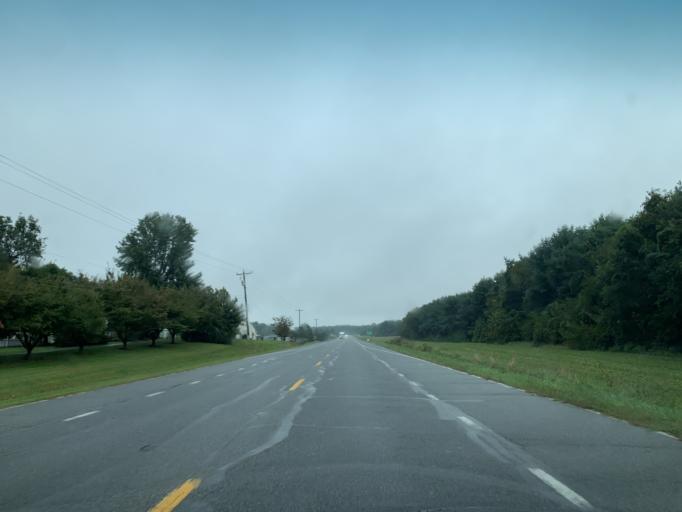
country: US
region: Delaware
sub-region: New Castle County
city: Townsend
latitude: 39.3345
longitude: -75.8757
